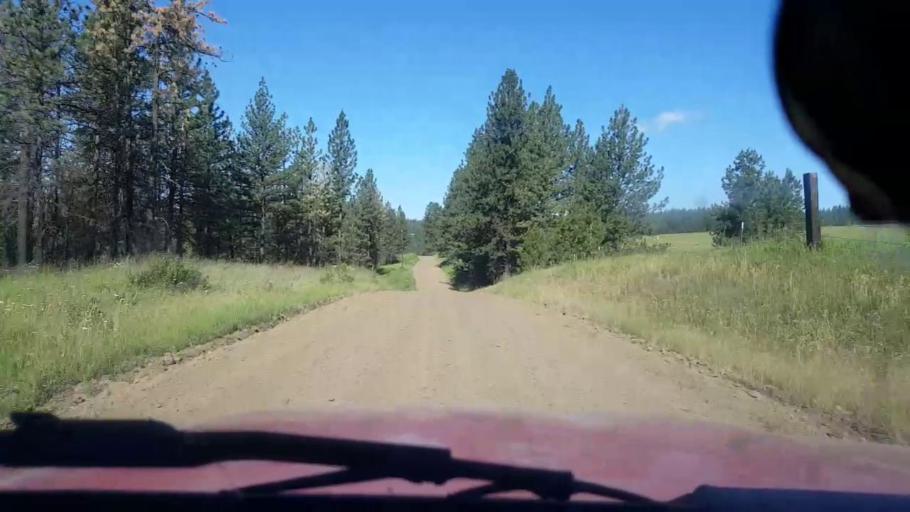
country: US
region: Washington
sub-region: Garfield County
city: Pomeroy
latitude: 45.9845
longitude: -117.4740
